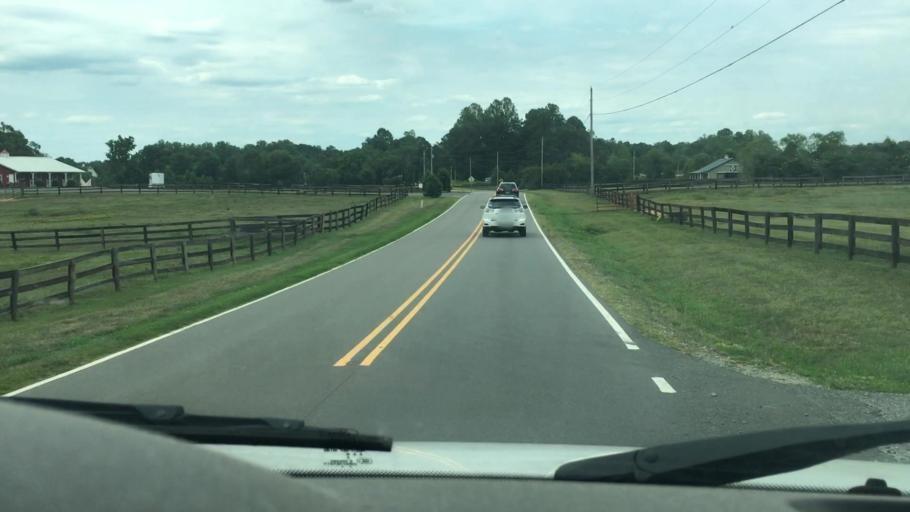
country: US
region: North Carolina
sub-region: Gaston County
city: Davidson
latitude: 35.4584
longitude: -80.7948
